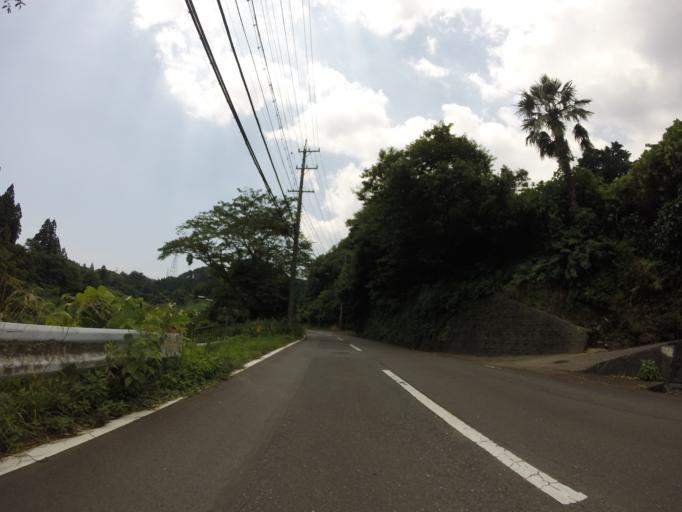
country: JP
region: Shizuoka
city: Kanaya
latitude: 34.8202
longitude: 138.0689
